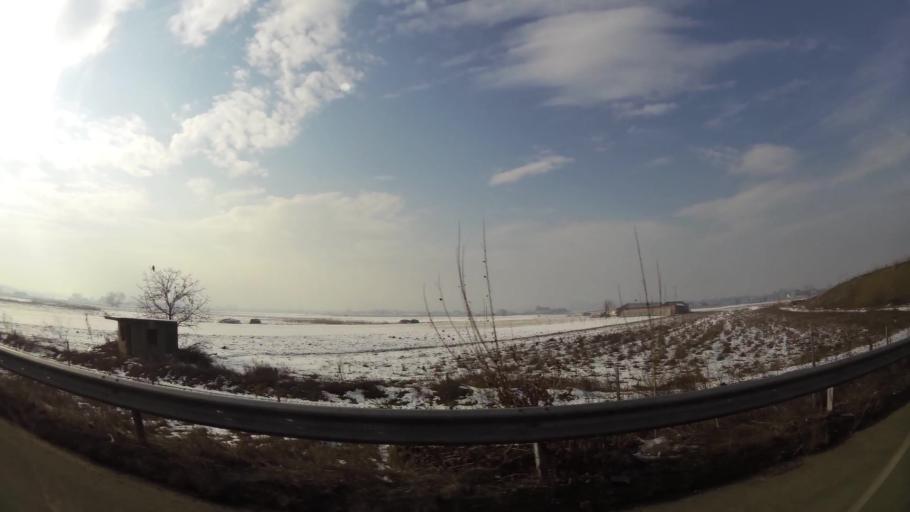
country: MK
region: Aracinovo
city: Arachinovo
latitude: 42.0066
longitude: 21.5350
